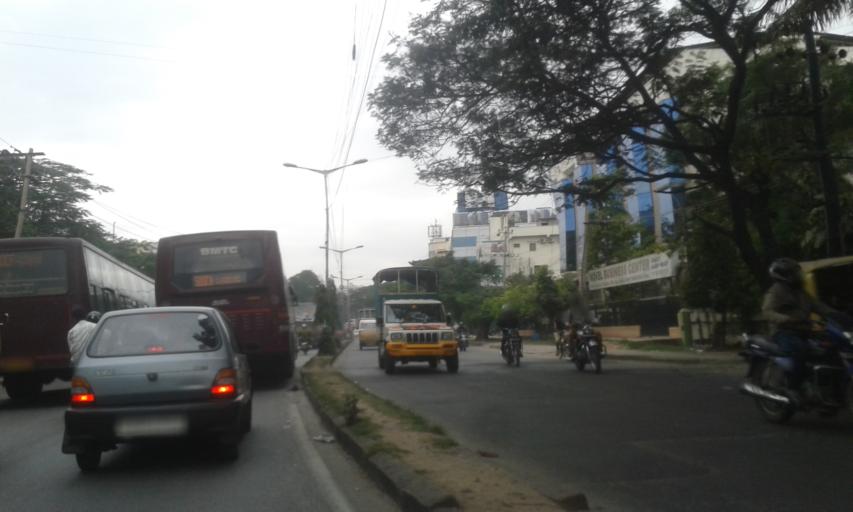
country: IN
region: Karnataka
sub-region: Bangalore Urban
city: Bangalore
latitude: 12.9163
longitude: 77.6196
